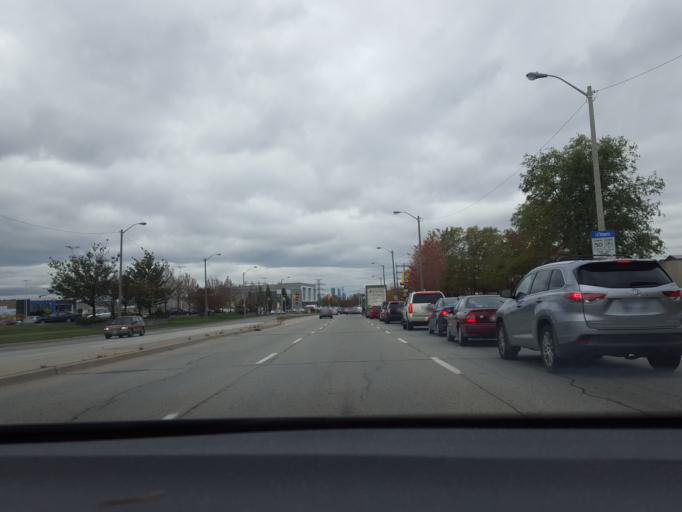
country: CA
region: Ontario
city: Etobicoke
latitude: 43.6149
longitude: -79.5535
